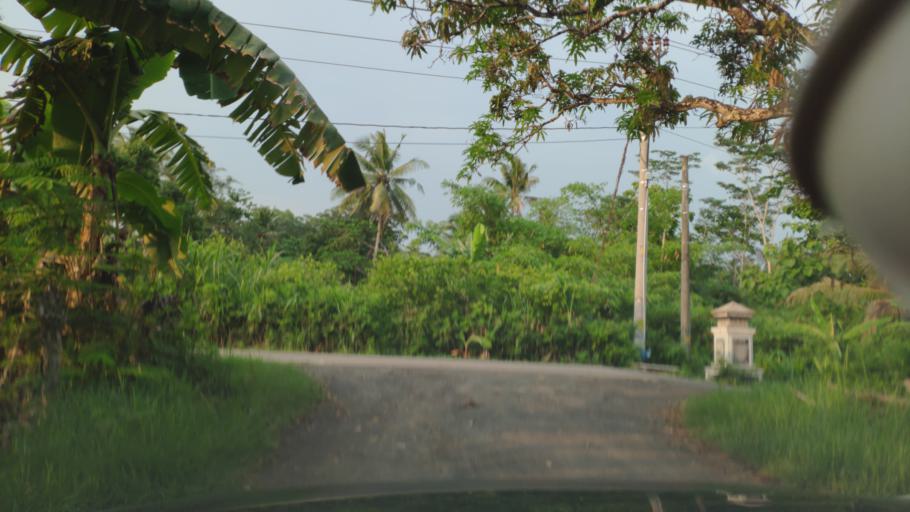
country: ID
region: Central Java
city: Jeruklegi
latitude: -7.6473
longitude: 108.9750
